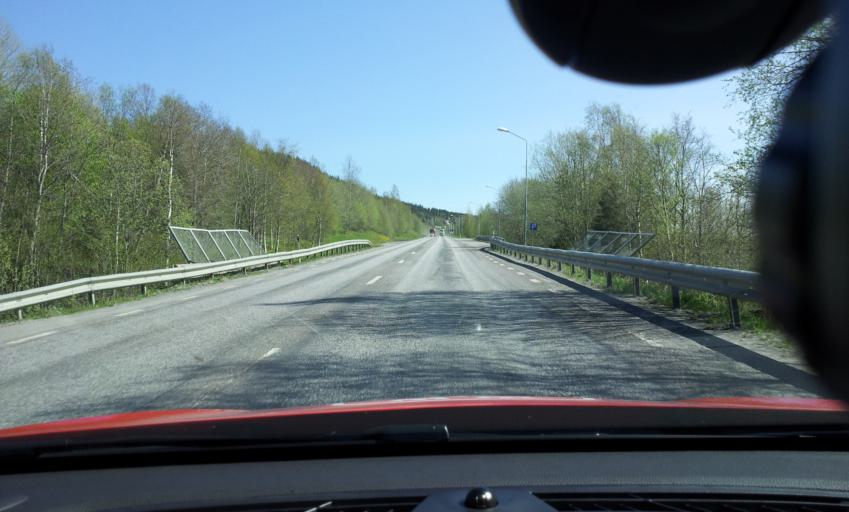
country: SE
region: Jaemtland
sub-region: Are Kommun
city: Are
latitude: 63.3831
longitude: 13.1368
